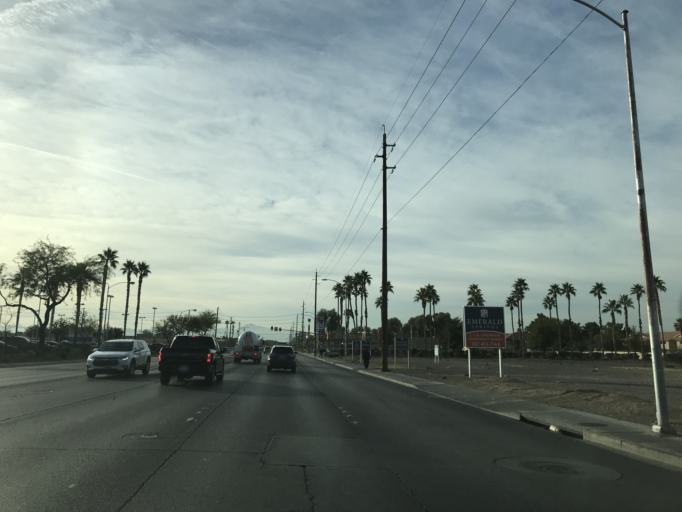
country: US
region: Nevada
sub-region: Clark County
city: Sunrise Manor
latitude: 36.1723
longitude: -115.0622
